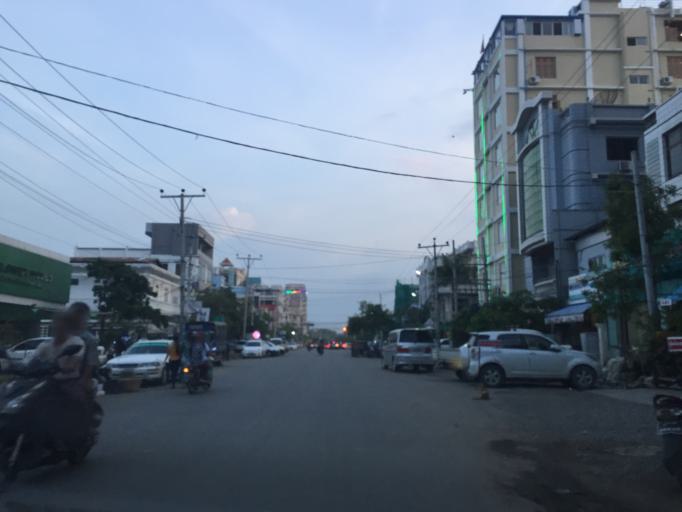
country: MM
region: Mandalay
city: Mandalay
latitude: 21.9705
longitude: 96.0882
